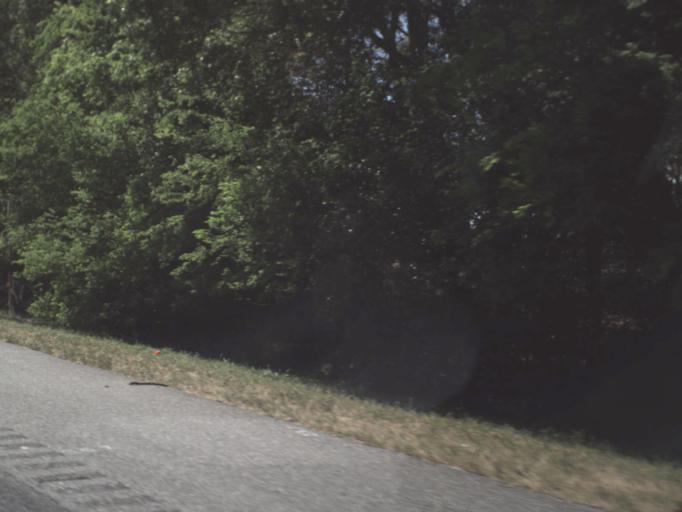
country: US
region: Florida
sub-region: Sumter County
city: Wildwood
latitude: 28.9143
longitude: -82.1116
